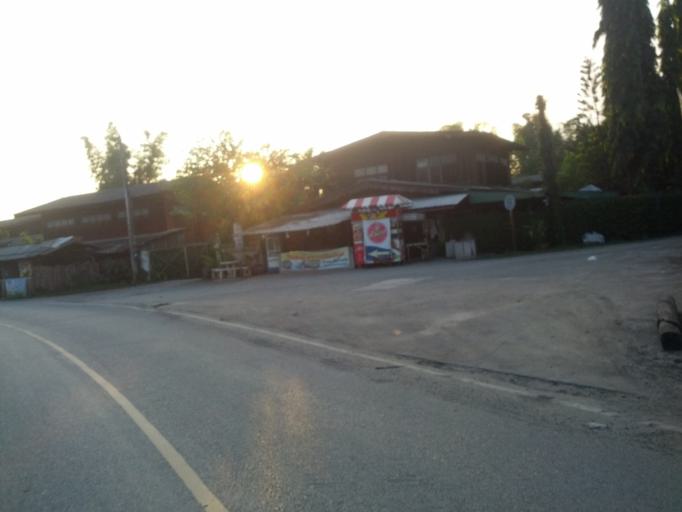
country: TH
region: Chiang Mai
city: San Kamphaeng
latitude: 18.7713
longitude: 99.1152
